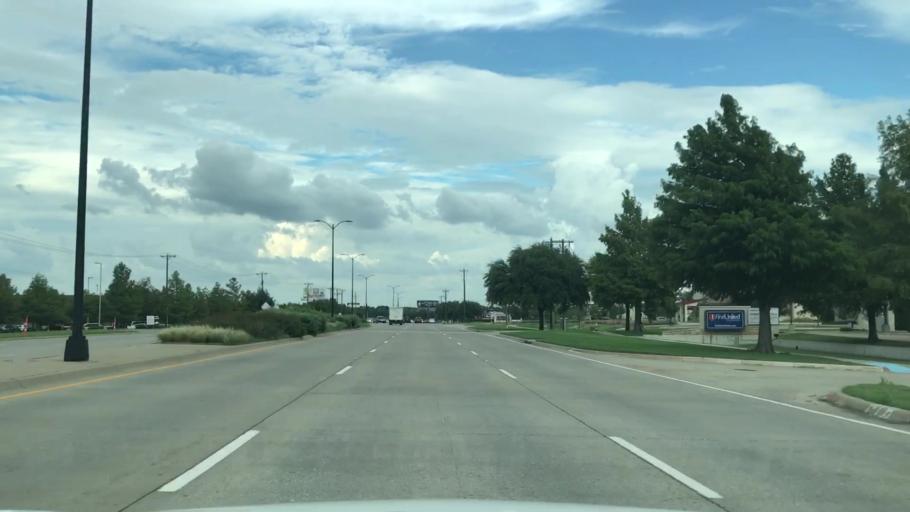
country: US
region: Texas
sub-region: Collin County
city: Frisco
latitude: 33.1292
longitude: -96.8048
